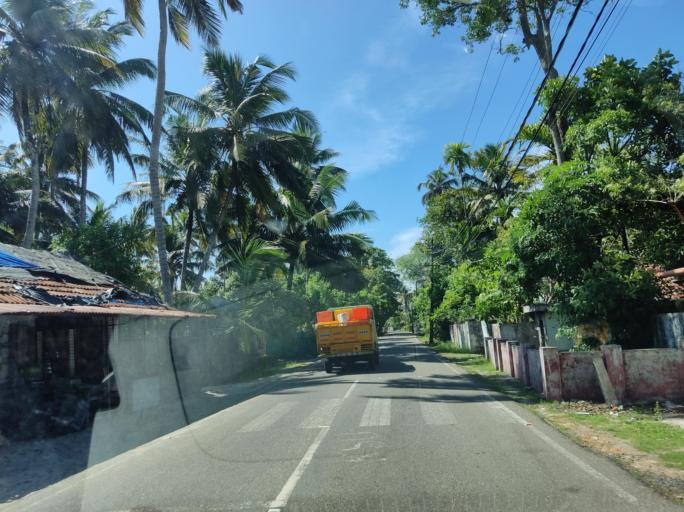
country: IN
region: Kerala
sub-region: Alappuzha
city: Kayankulam
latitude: 9.1782
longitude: 76.4445
